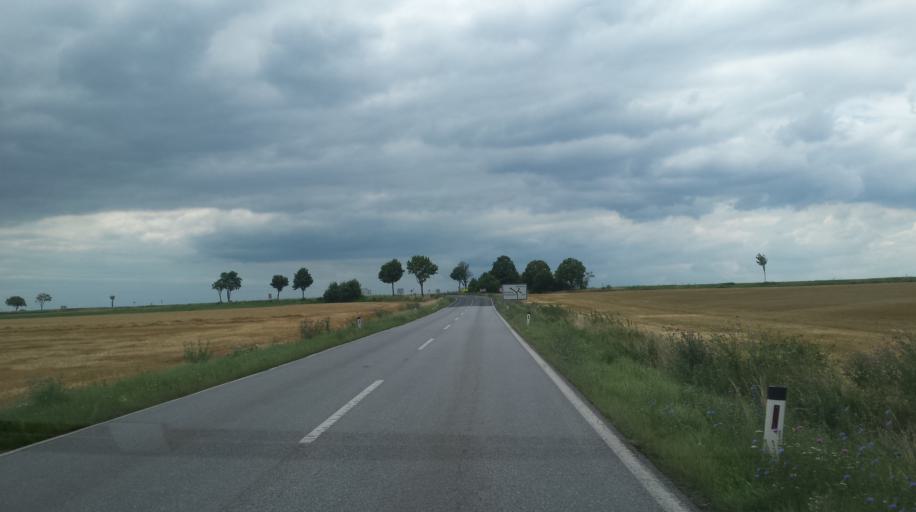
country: AT
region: Lower Austria
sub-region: Politischer Bezirk Wien-Umgebung
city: Moosbrunn
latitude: 48.0445
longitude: 16.4633
